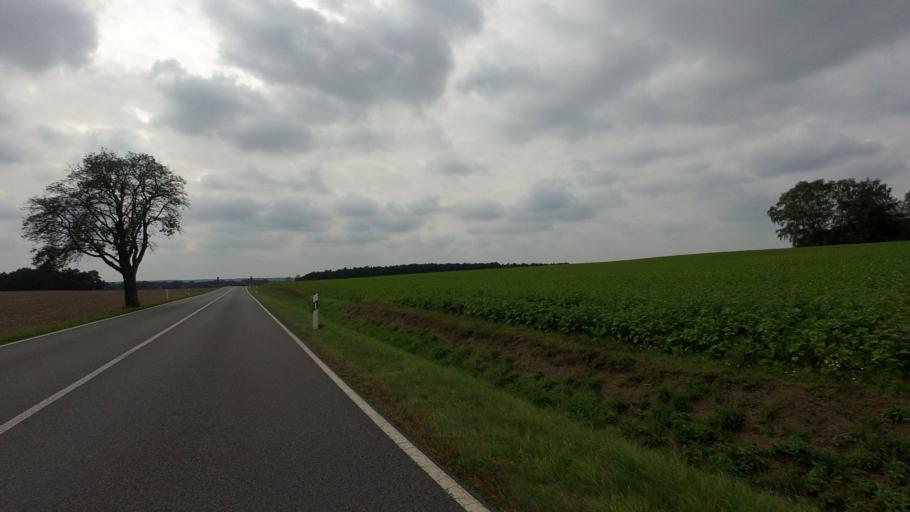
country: DE
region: Brandenburg
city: Luckau
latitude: 51.8240
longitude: 13.6834
